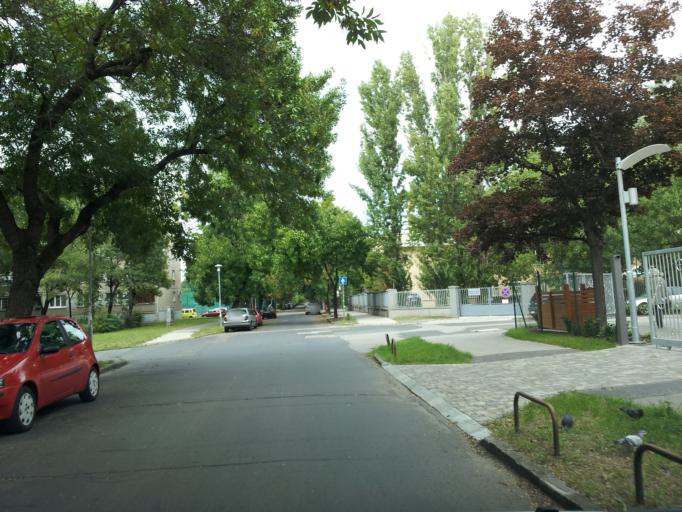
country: HU
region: Budapest
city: Budapest XI. keruelet
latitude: 47.4630
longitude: 19.0405
